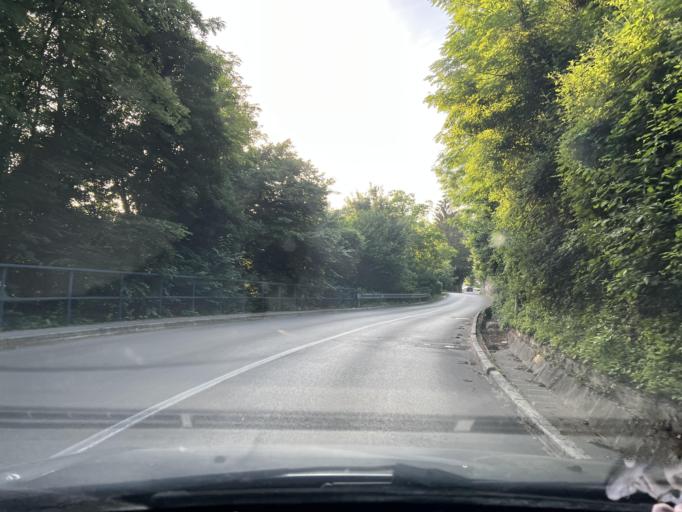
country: HR
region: Primorsko-Goranska
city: Drazice
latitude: 45.3839
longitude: 14.4468
